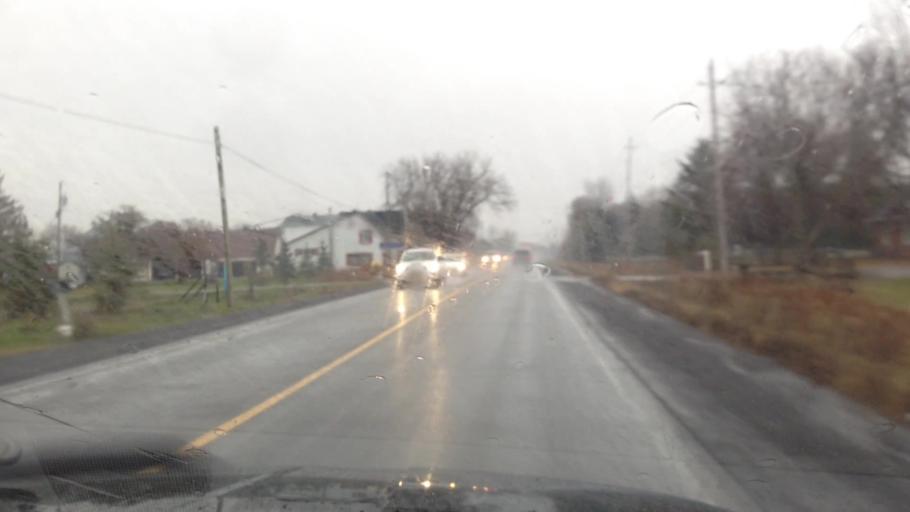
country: CA
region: Ontario
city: Bourget
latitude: 45.2997
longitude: -75.3280
